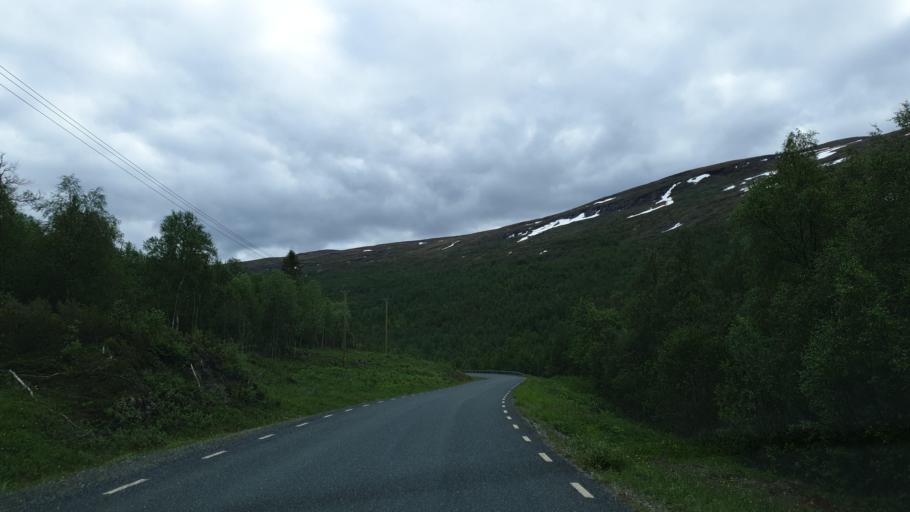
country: NO
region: Nordland
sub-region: Hattfjelldal
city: Hattfjelldal
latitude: 65.4257
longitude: 14.6026
